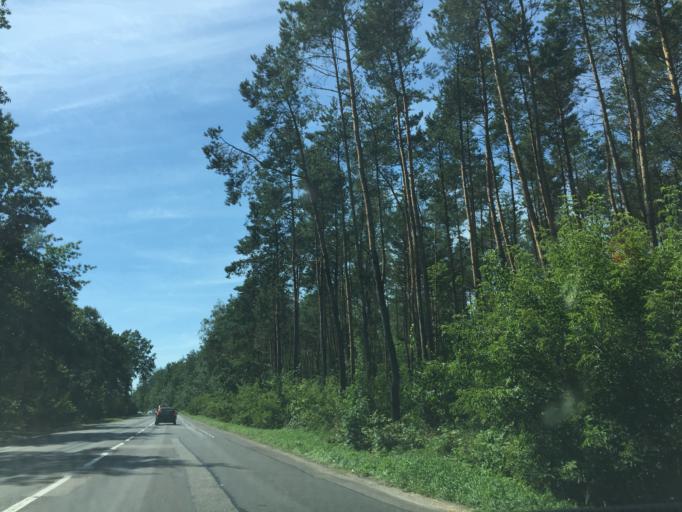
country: PL
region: Lodz Voivodeship
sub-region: Piotrkow Trybunalski
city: Piotrkow Trybunalski
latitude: 51.4288
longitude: 19.7154
